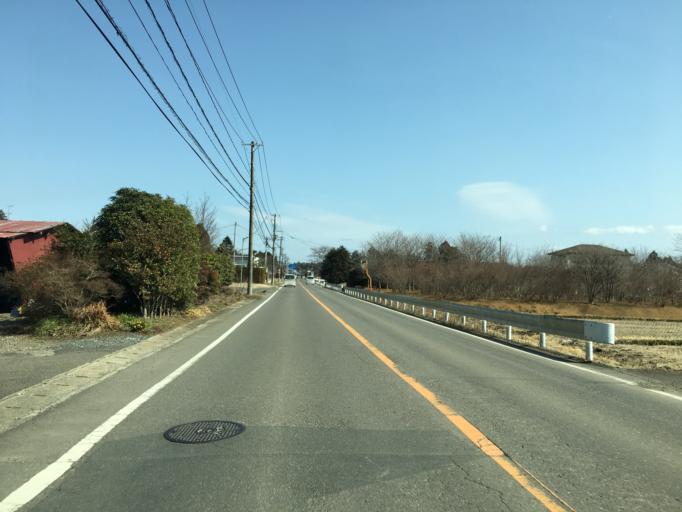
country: JP
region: Fukushima
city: Ishikawa
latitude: 37.1429
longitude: 140.3450
